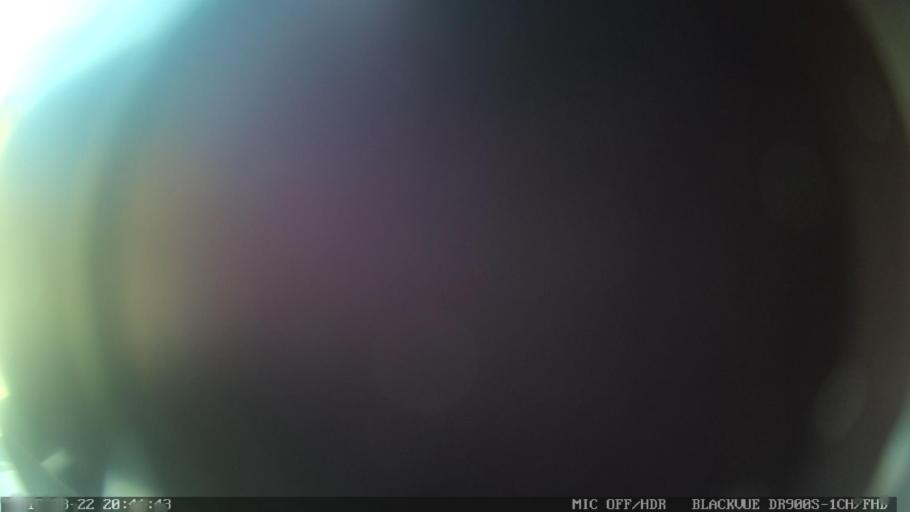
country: PT
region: Castelo Branco
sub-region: Proenca-A-Nova
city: Proenca-a-Nova
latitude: 39.6881
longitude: -7.8081
